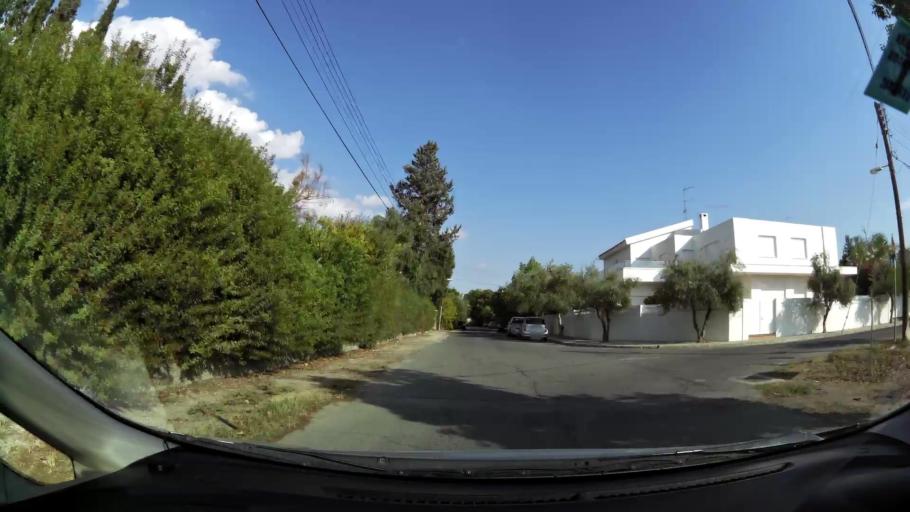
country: CY
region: Lefkosia
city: Nicosia
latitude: 35.1780
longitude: 33.3419
